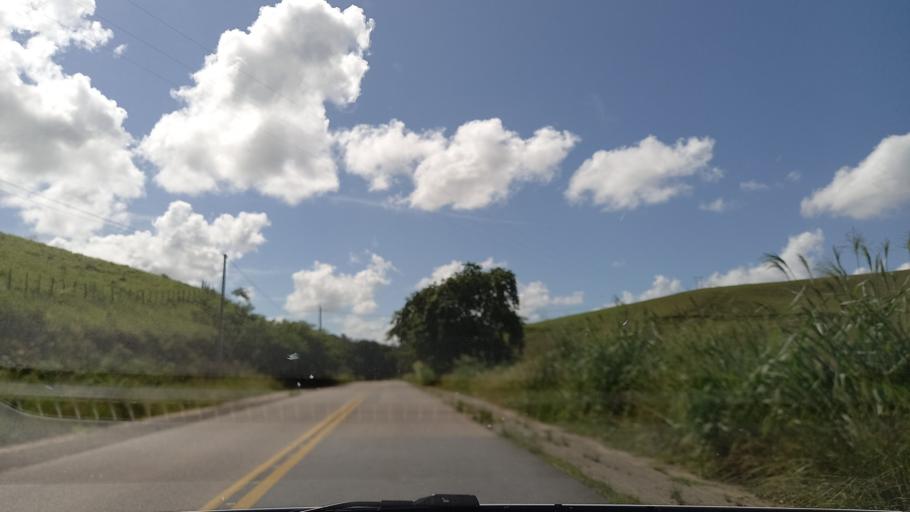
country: BR
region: Pernambuco
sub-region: Tamandare
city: Tamandare
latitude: -8.7469
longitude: -35.1712
